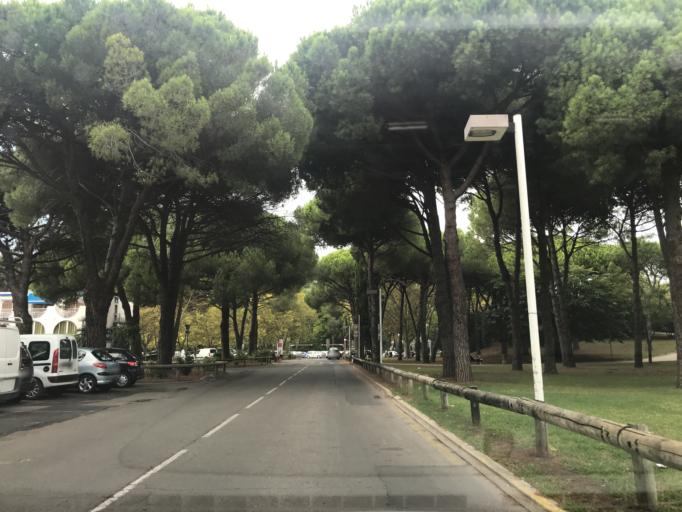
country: FR
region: Languedoc-Roussillon
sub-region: Departement de l'Herault
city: La Grande-Motte
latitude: 43.5623
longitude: 4.0845
